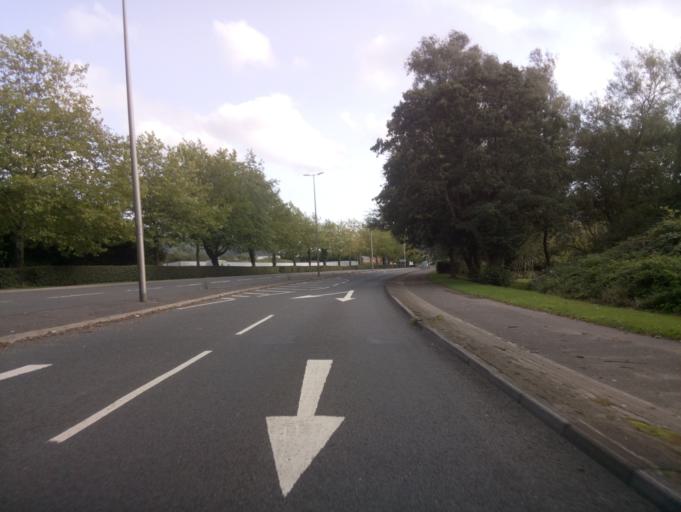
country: GB
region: Wales
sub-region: Caerphilly County Borough
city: Abertridwr
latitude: 51.5725
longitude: -3.2886
